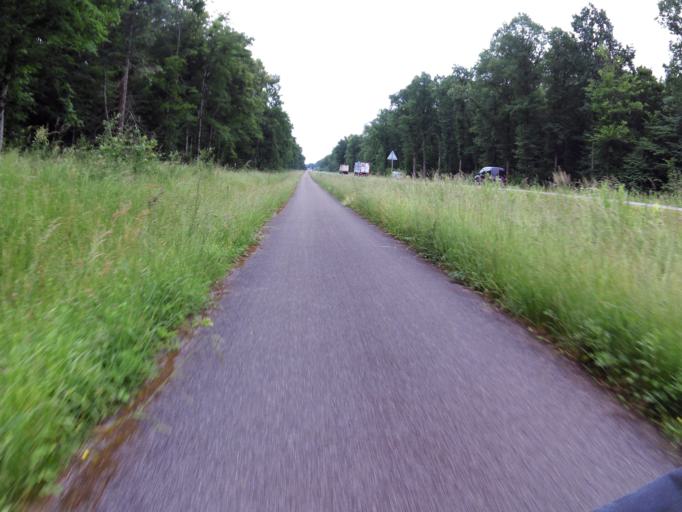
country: FR
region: Champagne-Ardenne
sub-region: Departement de la Haute-Marne
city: Laneuville-a-Remy
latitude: 48.5594
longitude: 4.8408
